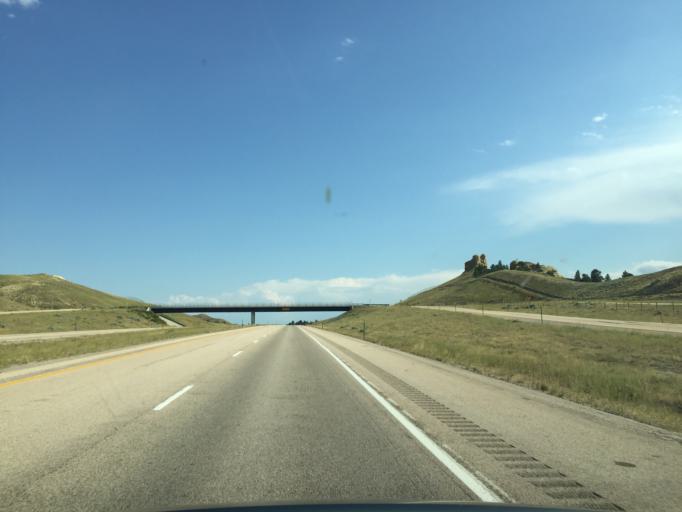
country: US
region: Wyoming
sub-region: Natrona County
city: Bar Nunn
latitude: 43.2493
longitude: -106.3878
